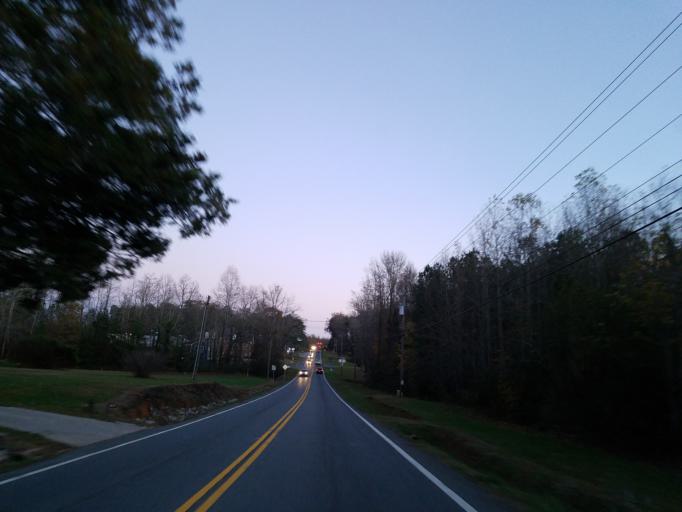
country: US
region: Georgia
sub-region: Dawson County
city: Dawsonville
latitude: 34.4150
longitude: -84.1121
